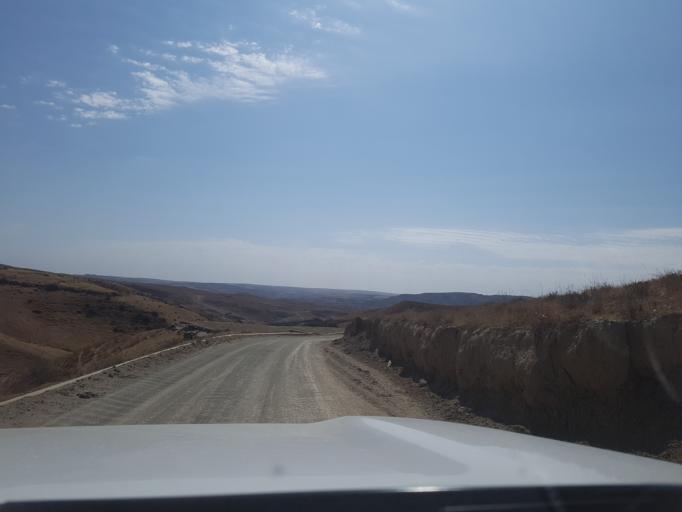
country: TM
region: Ahal
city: Baharly
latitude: 38.2499
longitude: 56.8920
